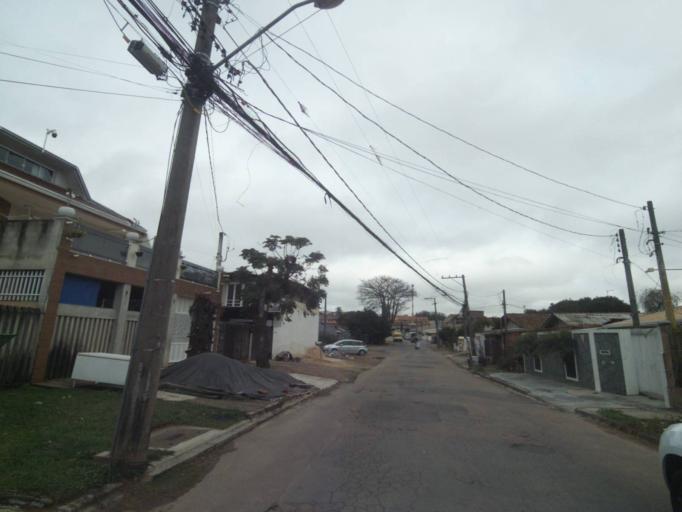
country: BR
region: Parana
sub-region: Curitiba
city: Curitiba
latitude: -25.5037
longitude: -49.2839
